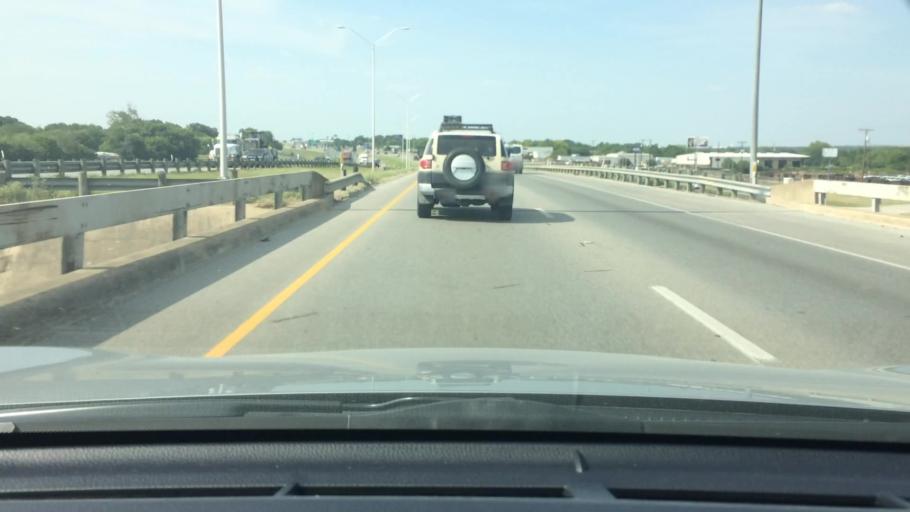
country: US
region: Texas
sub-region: Bexar County
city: China Grove
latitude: 29.3866
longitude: -98.3902
